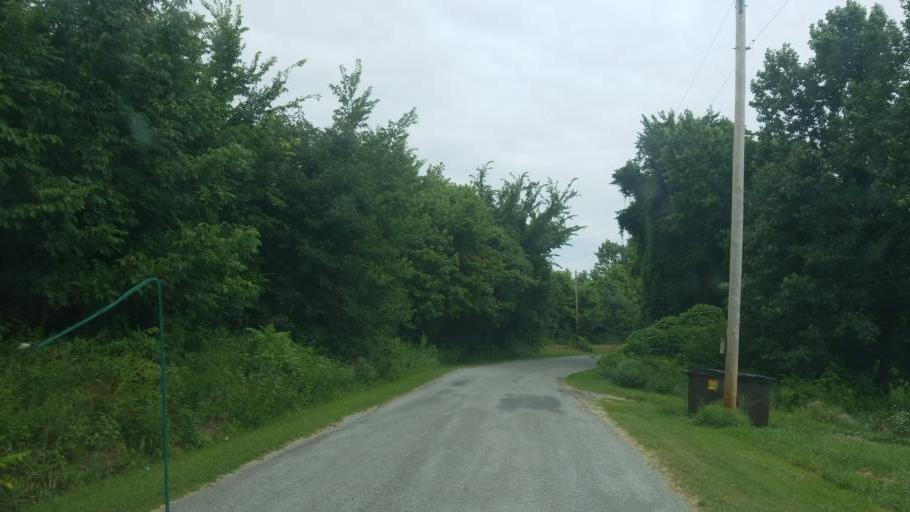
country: US
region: Illinois
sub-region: Jackson County
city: Murphysboro
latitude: 37.6745
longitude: -89.3906
